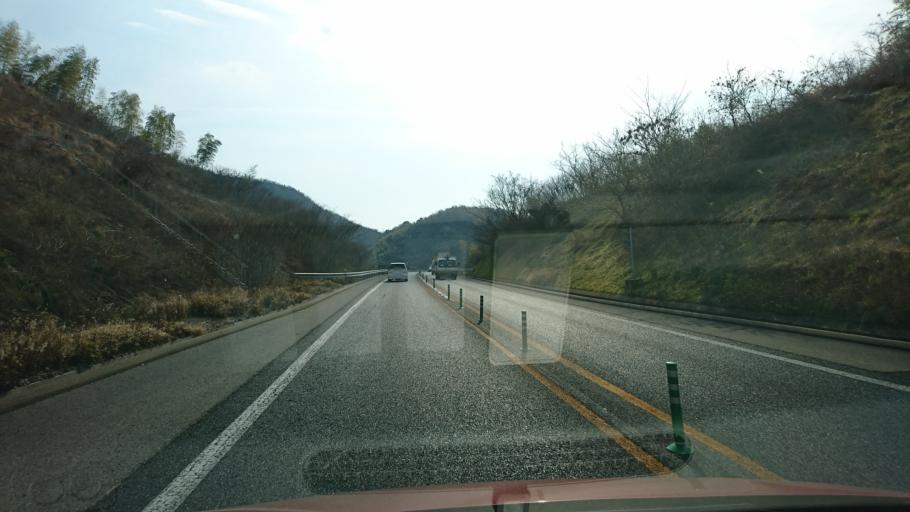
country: JP
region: Hiroshima
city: Innoshima
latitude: 34.3170
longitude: 133.1540
